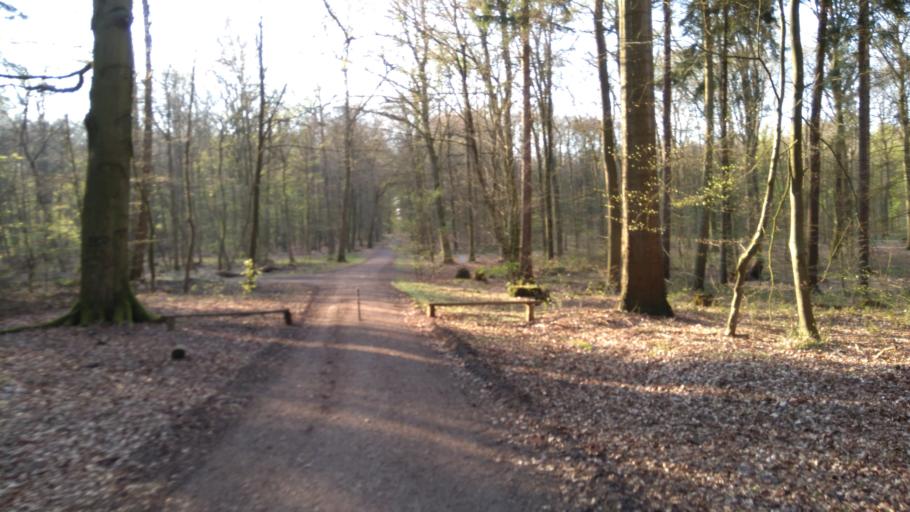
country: DE
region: Lower Saxony
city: Buxtehude
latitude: 53.4728
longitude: 9.6443
